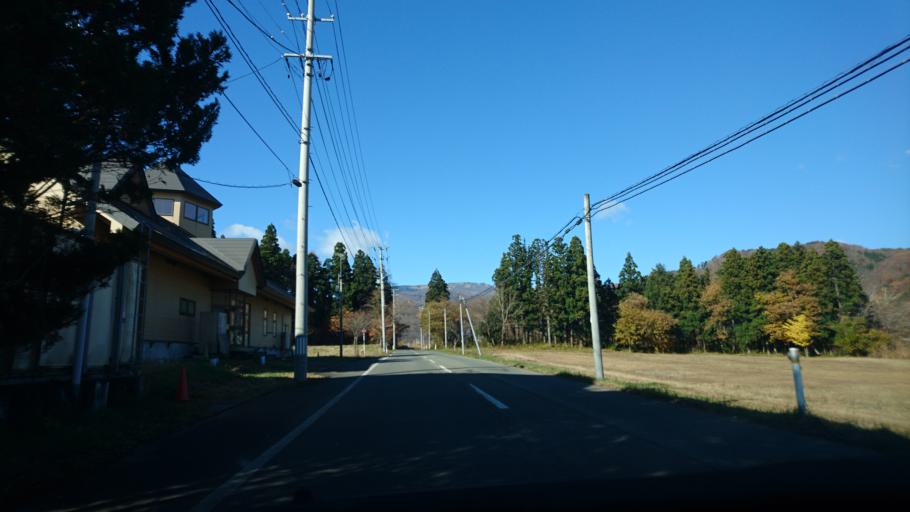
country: JP
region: Iwate
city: Mizusawa
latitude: 39.1182
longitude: 140.9379
